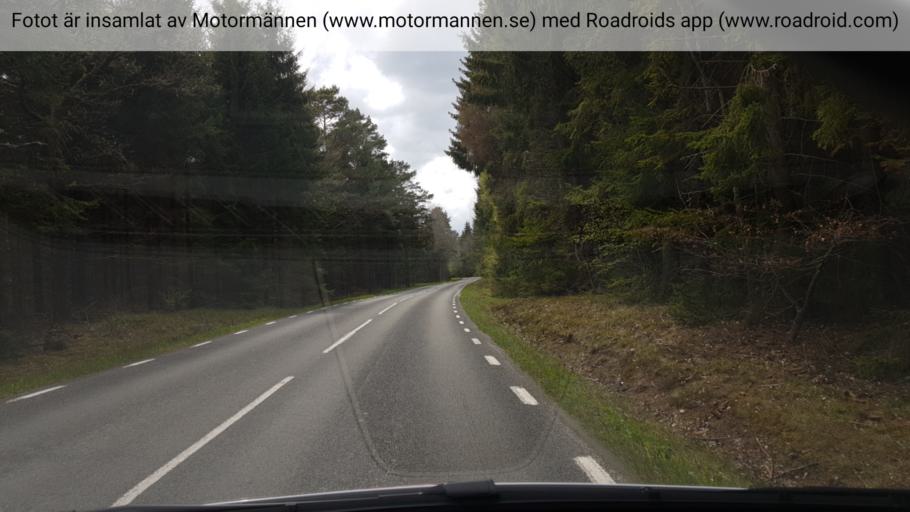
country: SE
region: Vaestra Goetaland
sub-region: Falkopings Kommun
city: Floby
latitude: 58.2233
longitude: 13.4047
